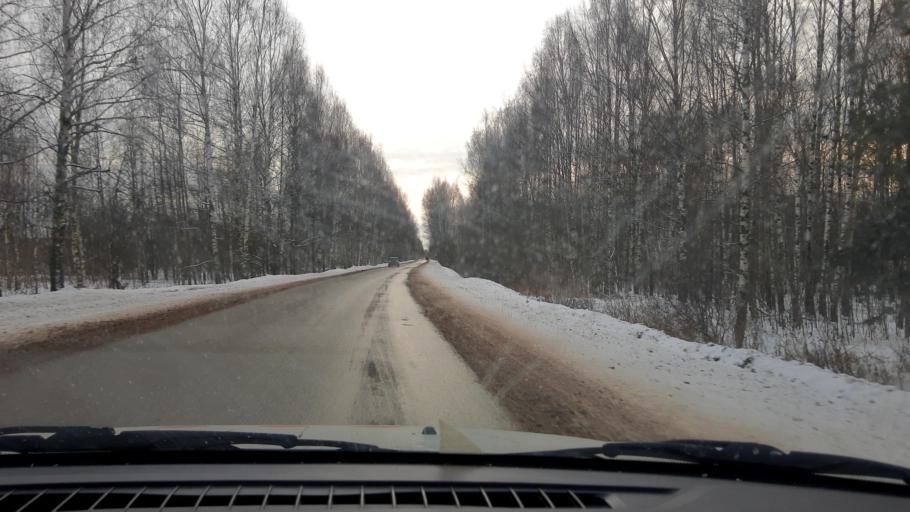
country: RU
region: Nizjnij Novgorod
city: Neklyudovo
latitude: 56.5209
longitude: 43.8361
